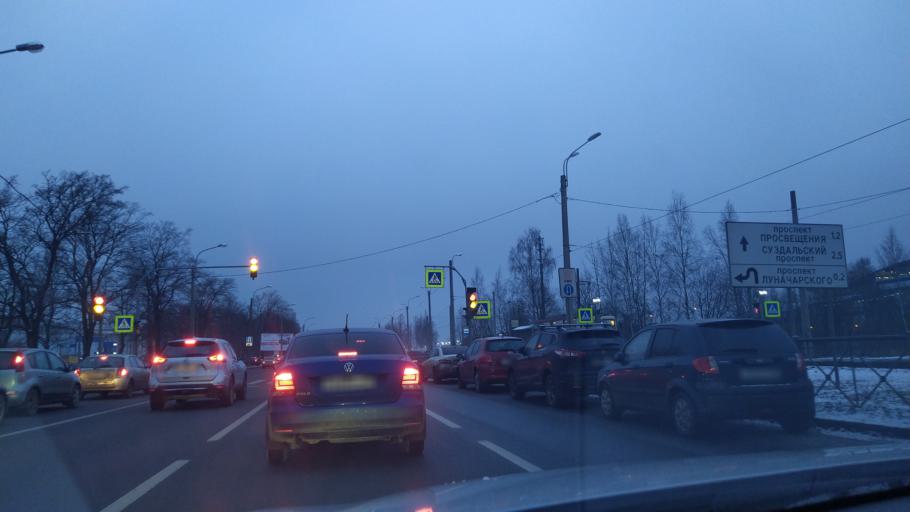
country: RU
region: St.-Petersburg
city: Grazhdanka
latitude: 60.0218
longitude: 30.4324
